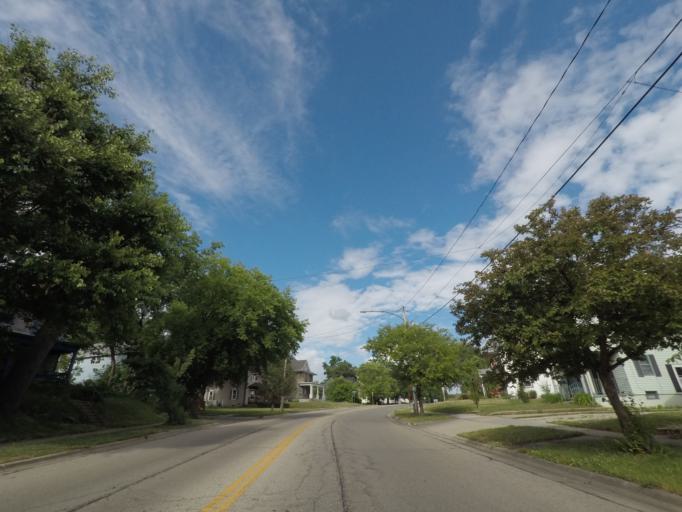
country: US
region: Wisconsin
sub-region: Rock County
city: Janesville
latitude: 42.6789
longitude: -89.0109
